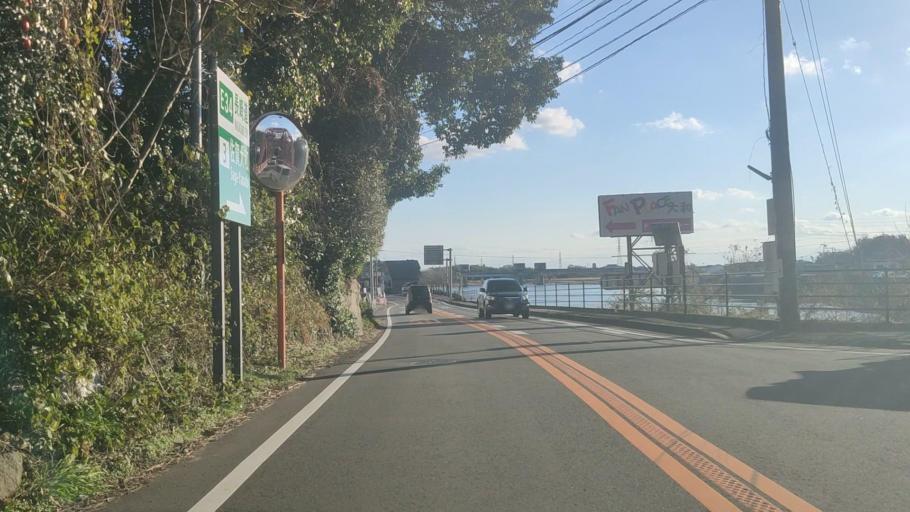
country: JP
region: Saga Prefecture
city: Saga-shi
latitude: 33.3271
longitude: 130.2692
